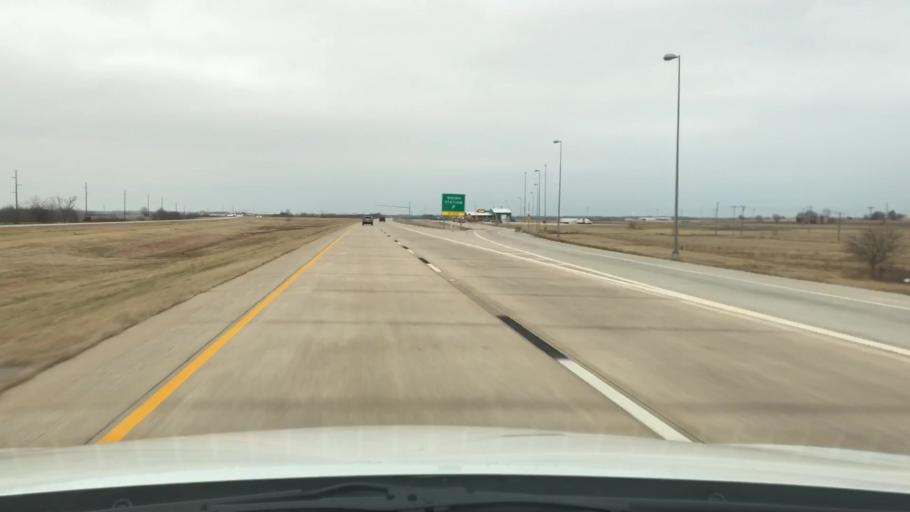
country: US
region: Oklahoma
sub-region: Love County
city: Marietta
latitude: 33.9004
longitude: -97.1344
